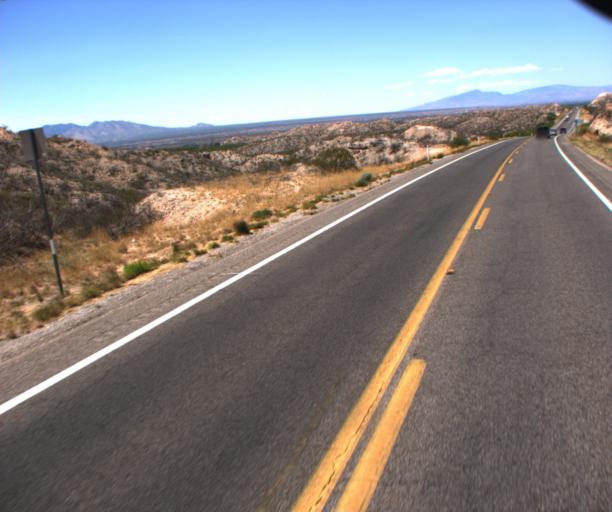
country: US
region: Arizona
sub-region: Cochise County
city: Saint David
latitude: 31.8218
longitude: -110.1735
